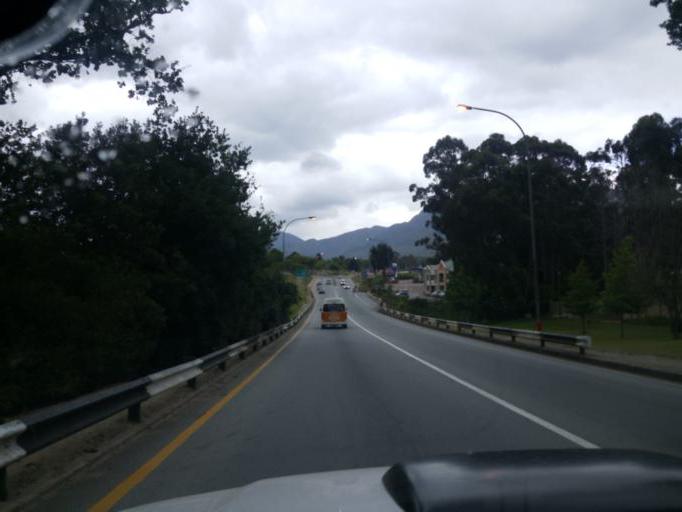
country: ZA
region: Western Cape
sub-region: Eden District Municipality
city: George
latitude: -33.9515
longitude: 22.4367
